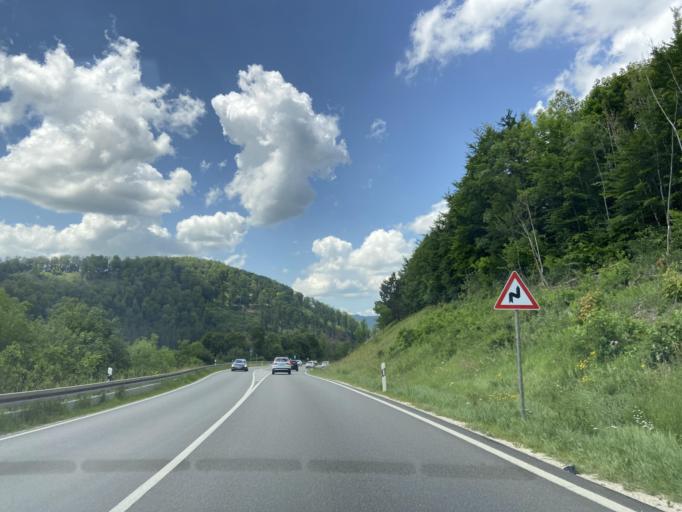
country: DE
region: Baden-Wuerttemberg
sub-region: Tuebingen Region
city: Strassberg
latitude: 48.1869
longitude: 9.0933
